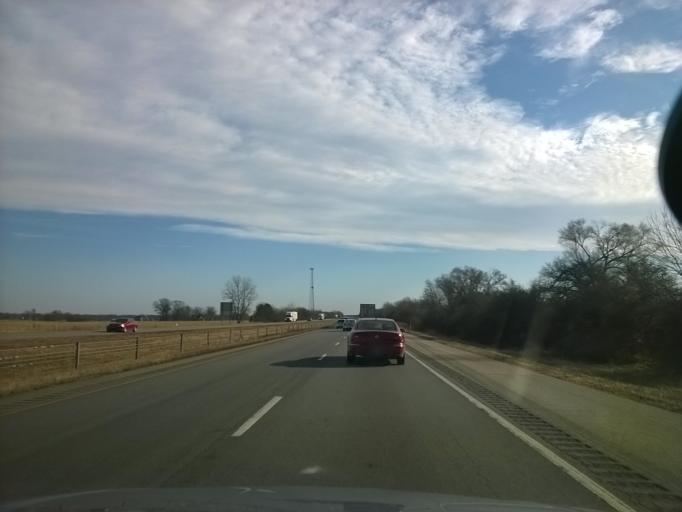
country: US
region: Indiana
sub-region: Johnson County
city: Franklin
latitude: 39.4630
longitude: -86.0039
